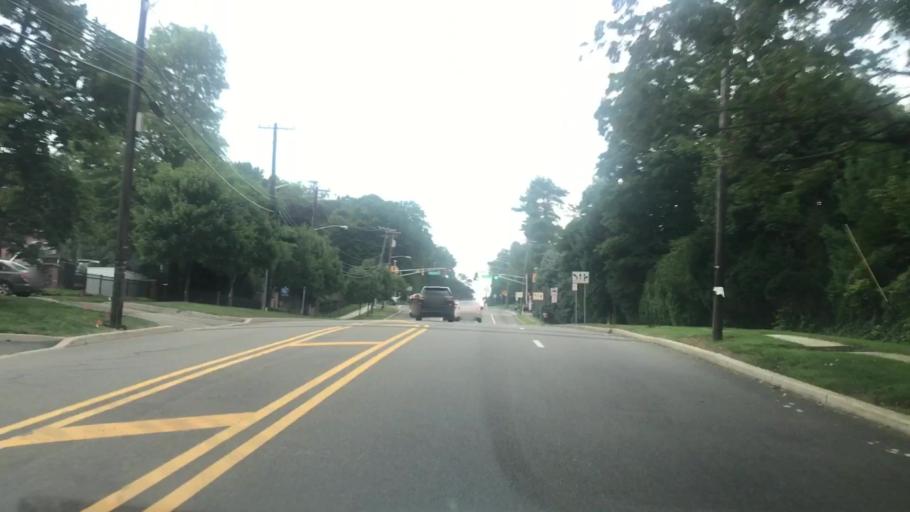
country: US
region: New Jersey
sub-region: Bergen County
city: Englewood Cliffs
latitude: 40.8870
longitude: -73.9626
